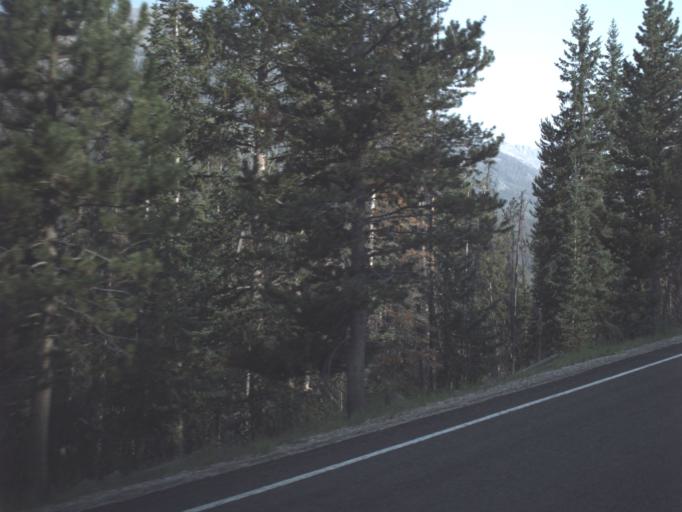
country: US
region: Utah
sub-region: Summit County
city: Kamas
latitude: 40.7782
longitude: -110.8851
